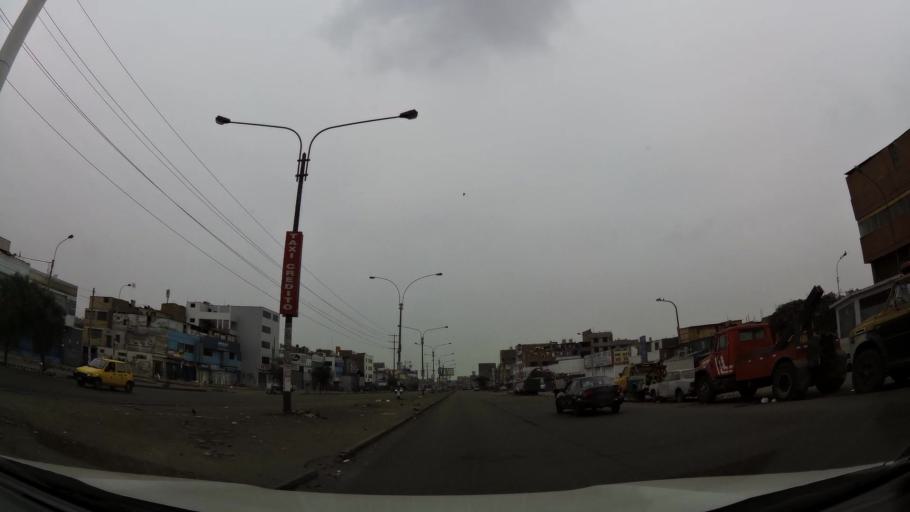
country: PE
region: Lima
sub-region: Lima
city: San Luis
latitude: -12.0734
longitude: -77.0055
